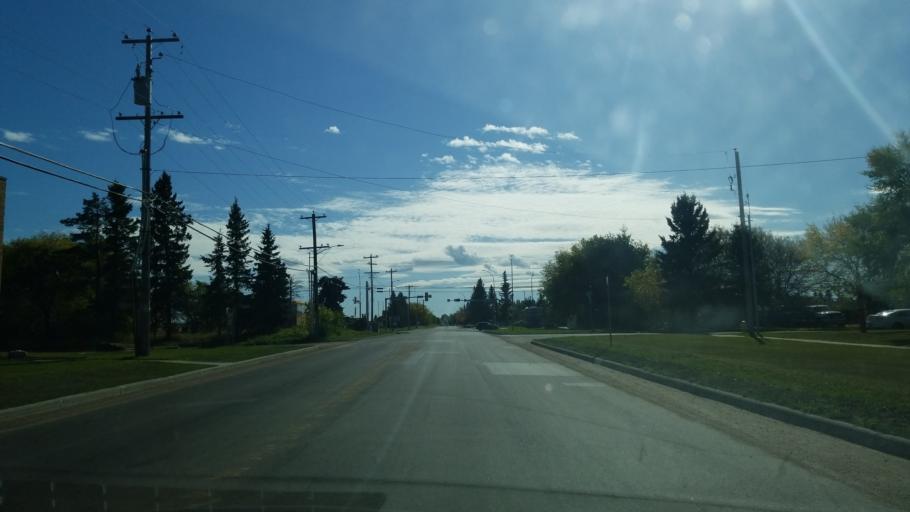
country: CA
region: Saskatchewan
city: Lloydminster
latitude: 53.2793
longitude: -109.9914
